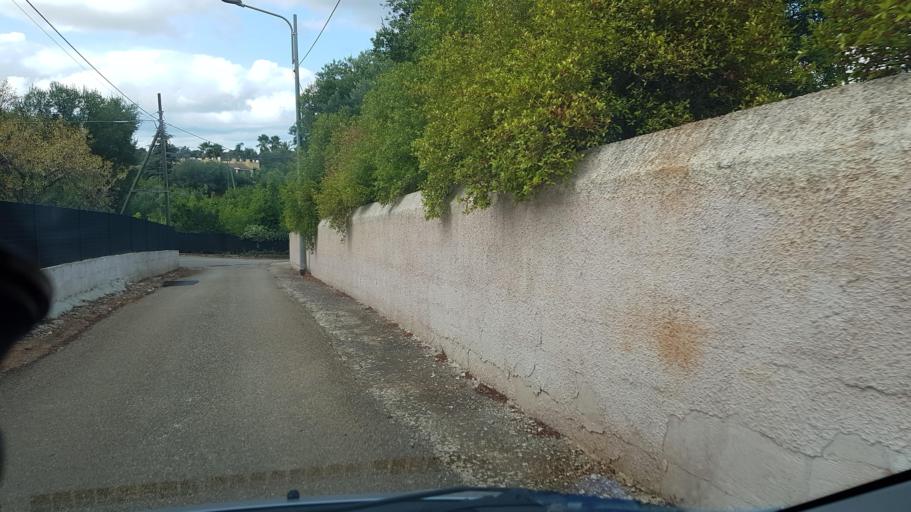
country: IT
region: Apulia
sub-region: Provincia di Brindisi
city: San Vito dei Normanni
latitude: 40.6671
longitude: 17.7215
